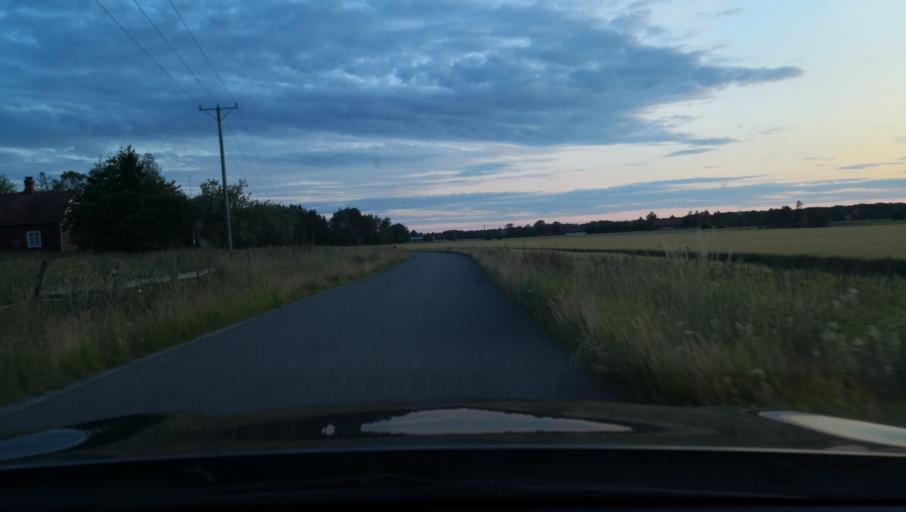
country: SE
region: Uppsala
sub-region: Osthammars Kommun
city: Bjorklinge
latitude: 60.0380
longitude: 17.4977
